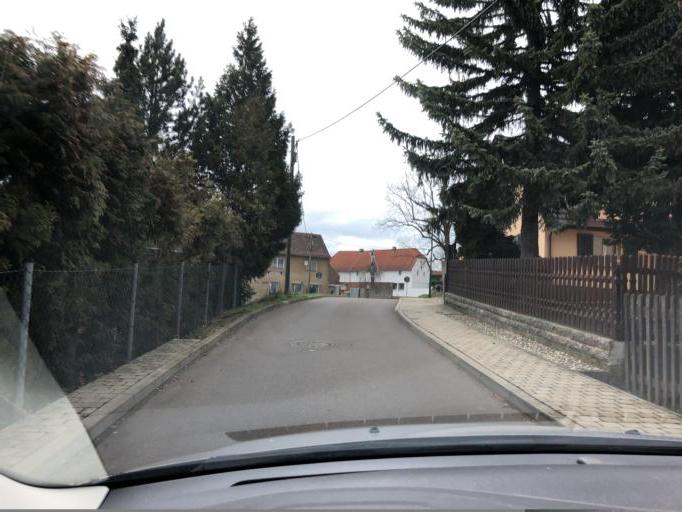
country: DE
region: Saxony-Anhalt
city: Muschwitz
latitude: 51.1894
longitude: 12.1310
